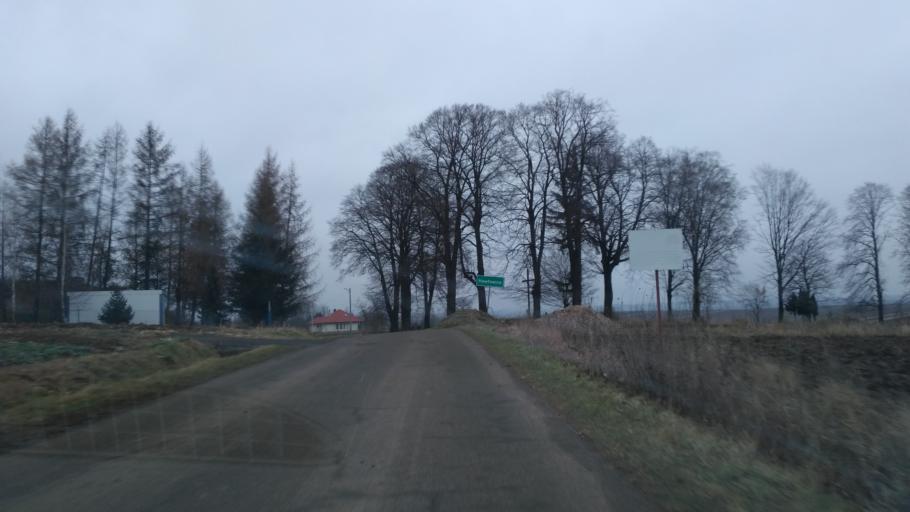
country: PL
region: Subcarpathian Voivodeship
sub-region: Powiat jaroslawski
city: Pruchnik
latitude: 49.9196
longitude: 22.5347
